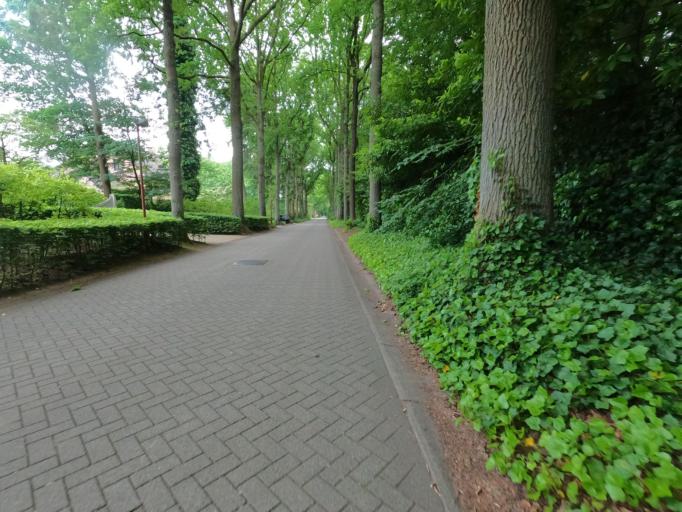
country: BE
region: Flanders
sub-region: Provincie Antwerpen
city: Kalmthout
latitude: 51.3614
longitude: 4.4704
